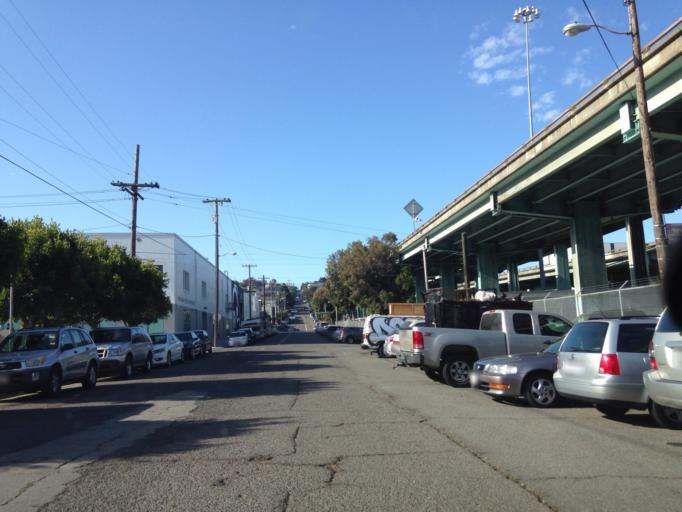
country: US
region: California
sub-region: San Francisco County
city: San Francisco
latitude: 37.7677
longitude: -122.4048
